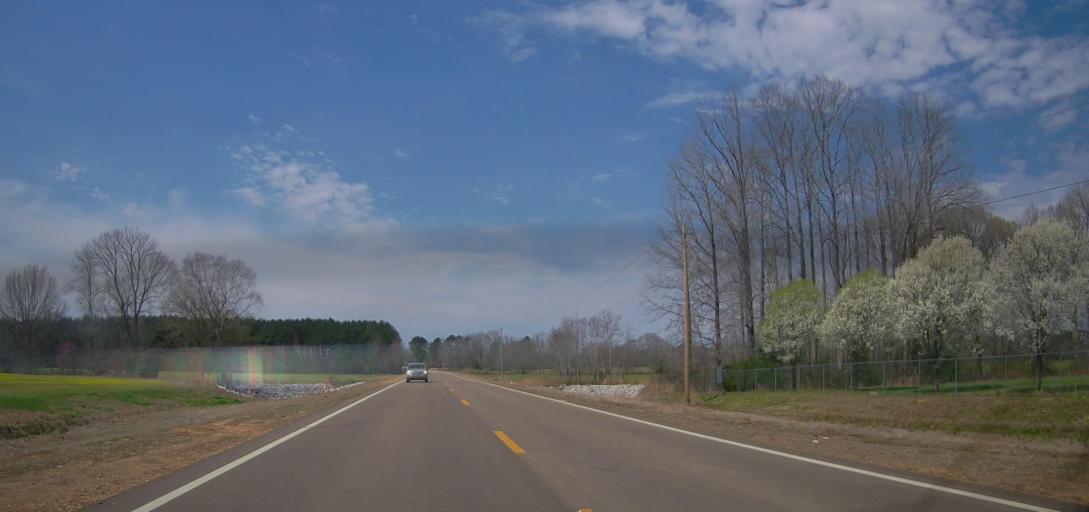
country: US
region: Mississippi
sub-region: Union County
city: New Albany
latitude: 34.6166
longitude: -89.1711
